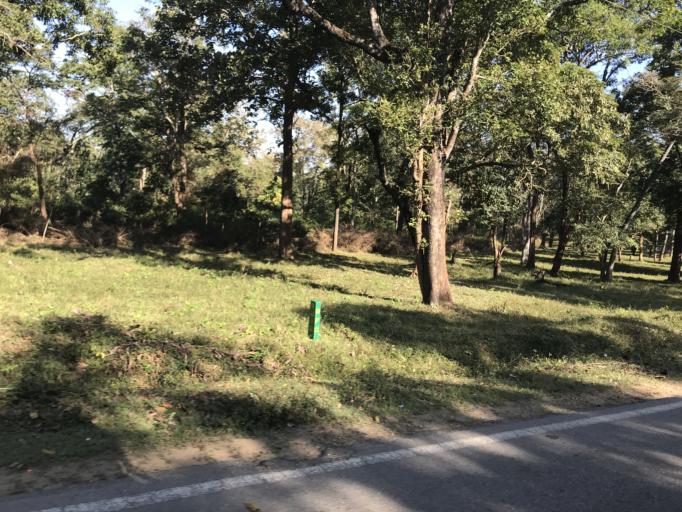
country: IN
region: Karnataka
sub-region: Mysore
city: Heggadadevankote
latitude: 11.9459
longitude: 76.2303
